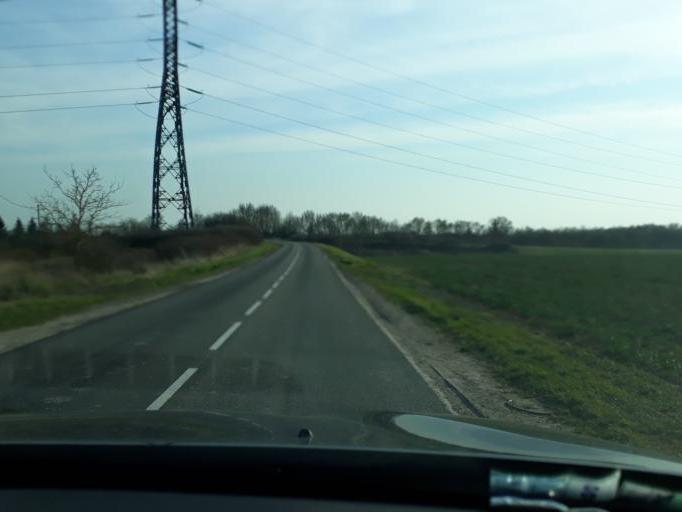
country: FR
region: Centre
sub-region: Departement du Loiret
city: Meung-sur-Loire
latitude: 47.8493
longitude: 1.6817
